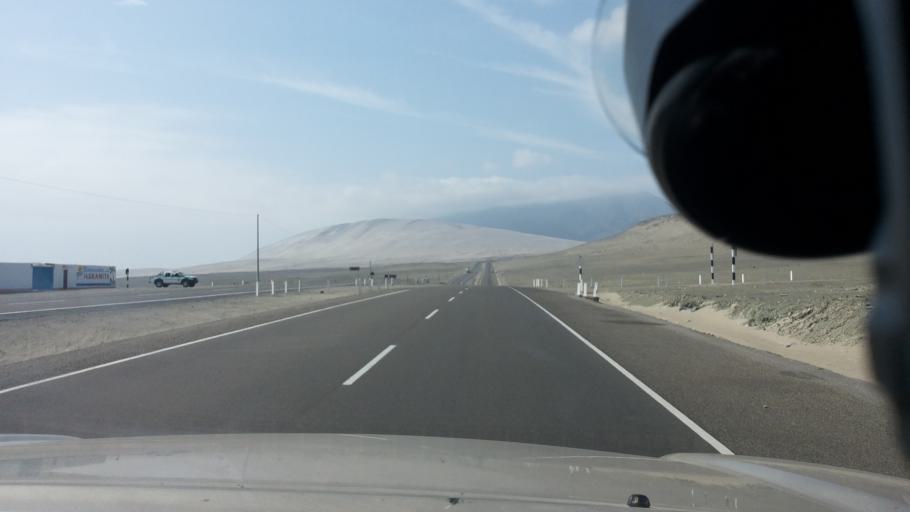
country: PE
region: Ancash
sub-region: Provincia de Casma
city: Casma
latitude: -9.7054
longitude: -78.2766
